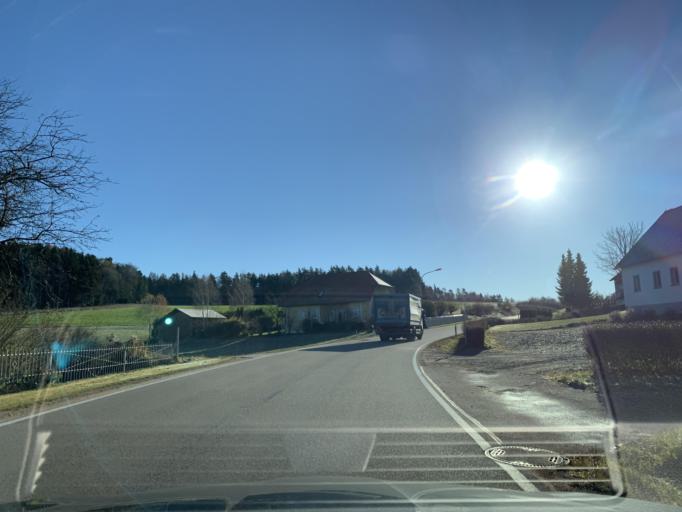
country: DE
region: Bavaria
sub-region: Upper Palatinate
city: Oberviechtach
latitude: 49.4400
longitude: 12.4165
